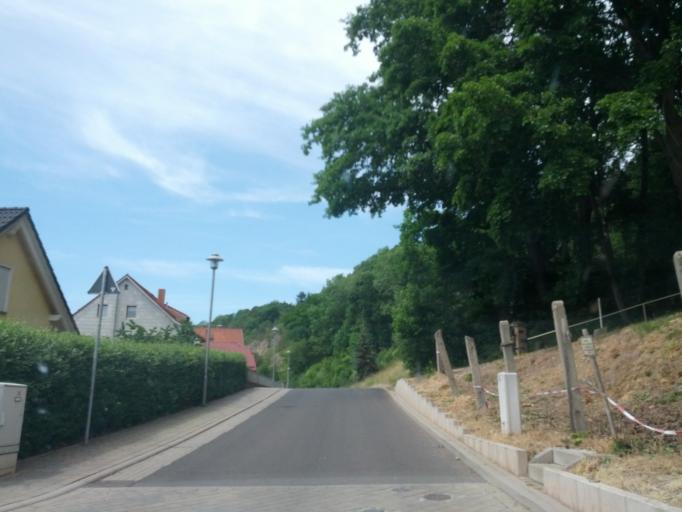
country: DE
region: Thuringia
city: Thal
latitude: 50.9581
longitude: 10.4002
